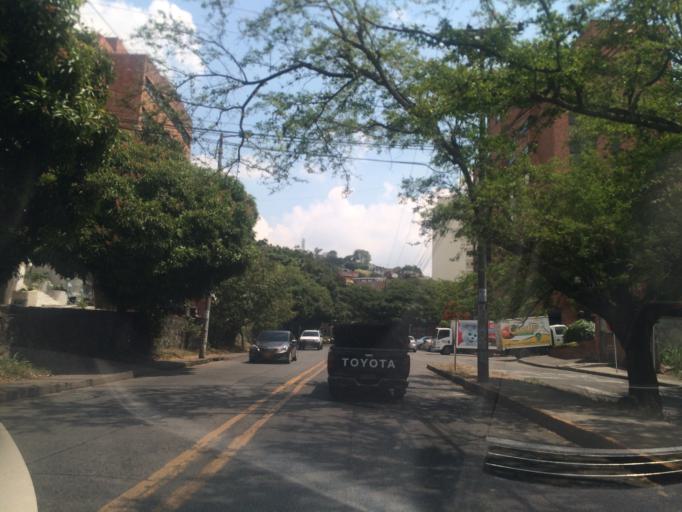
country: CO
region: Valle del Cauca
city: Cali
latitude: 3.4397
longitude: -76.5469
